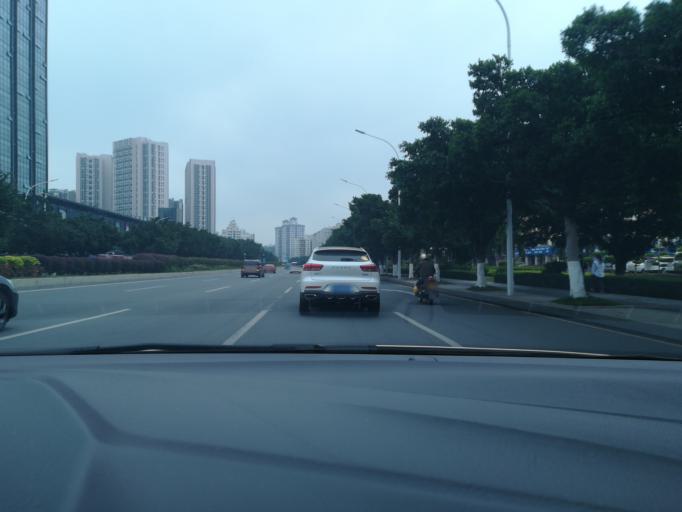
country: CN
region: Guangdong
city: Nansha
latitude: 22.8021
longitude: 113.5493
